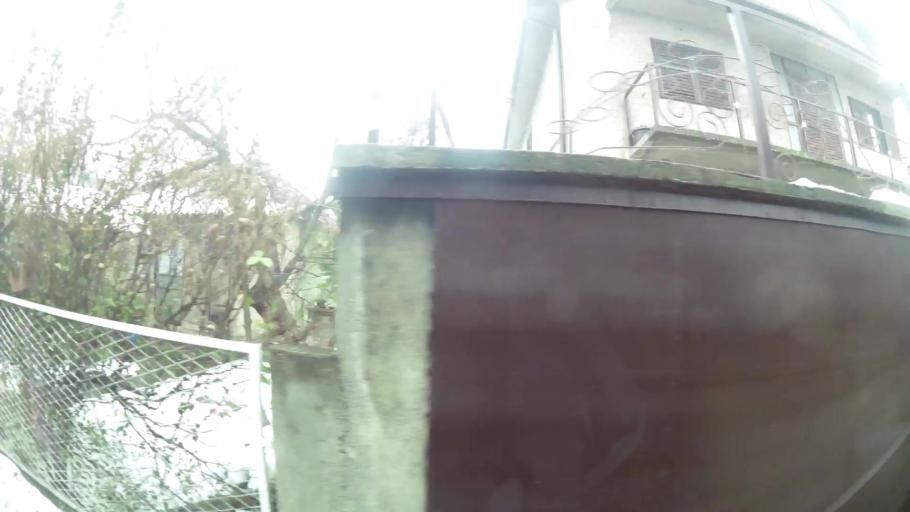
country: RS
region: Central Serbia
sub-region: Belgrade
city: Zvezdara
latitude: 44.7803
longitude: 20.5301
